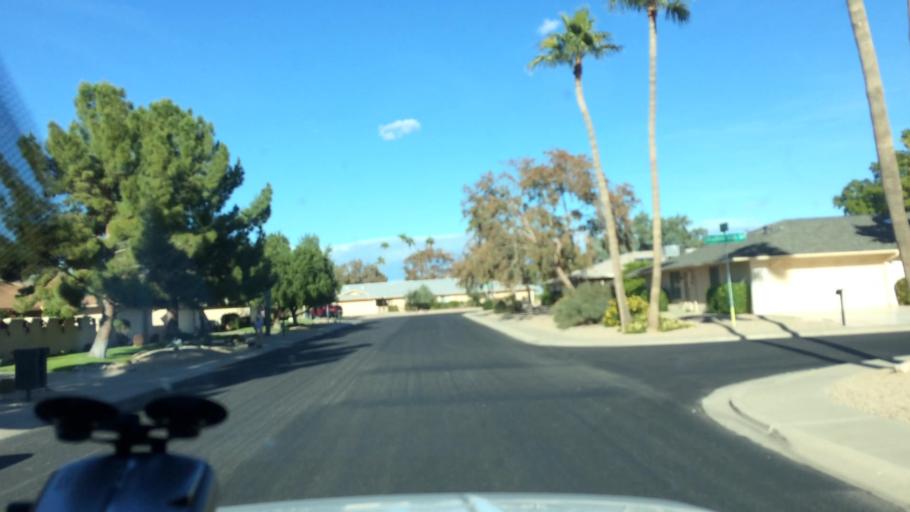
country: US
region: Arizona
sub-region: Maricopa County
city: Sun City West
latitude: 33.6550
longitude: -112.3375
